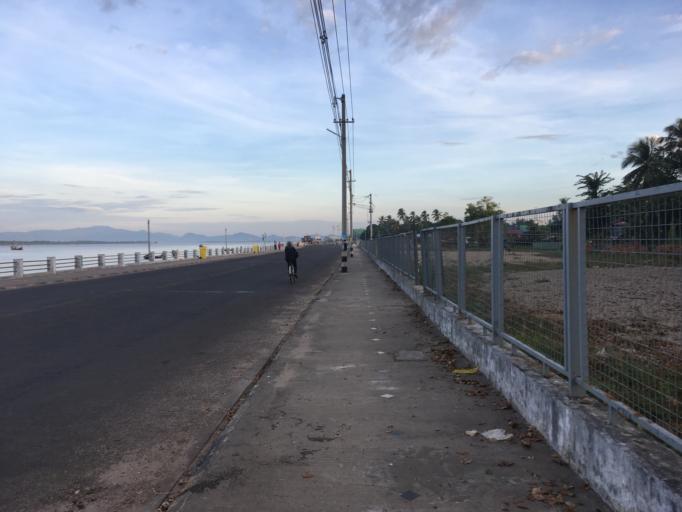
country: MM
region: Mon
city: Mawlamyine
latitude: 16.4605
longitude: 97.6231
